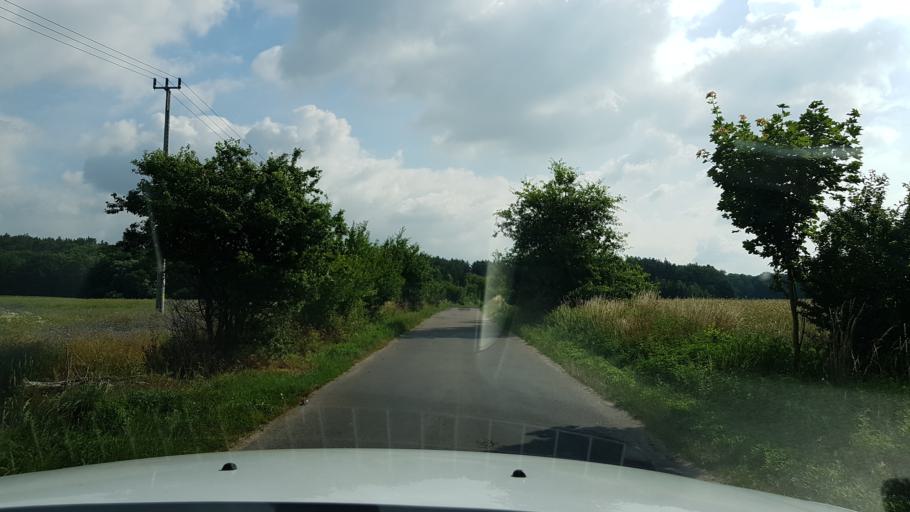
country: PL
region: West Pomeranian Voivodeship
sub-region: Powiat gryfinski
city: Gryfino
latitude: 53.2101
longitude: 14.5857
